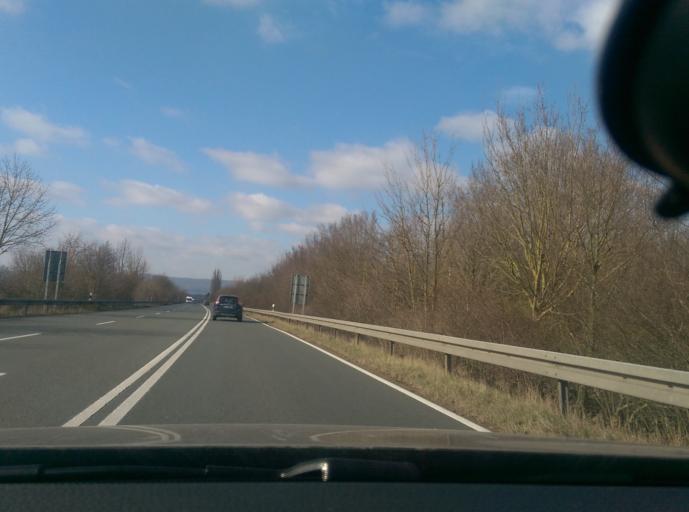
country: DE
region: Lower Saxony
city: Hessisch Oldendorf
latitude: 52.1461
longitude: 9.2875
